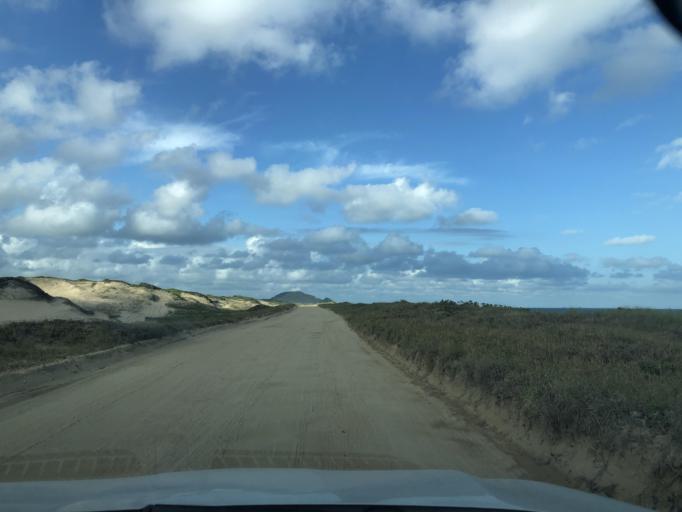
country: BR
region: Santa Catarina
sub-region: Sao Francisco Do Sul
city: Sao Francisco do Sul
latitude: -26.2616
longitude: -48.5197
